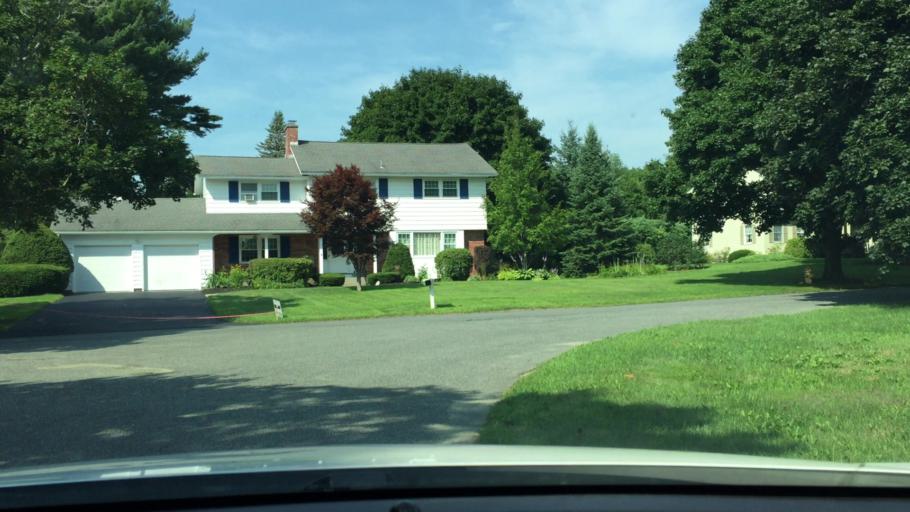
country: US
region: Massachusetts
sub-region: Berkshire County
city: Pittsfield
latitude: 42.4195
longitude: -73.2438
